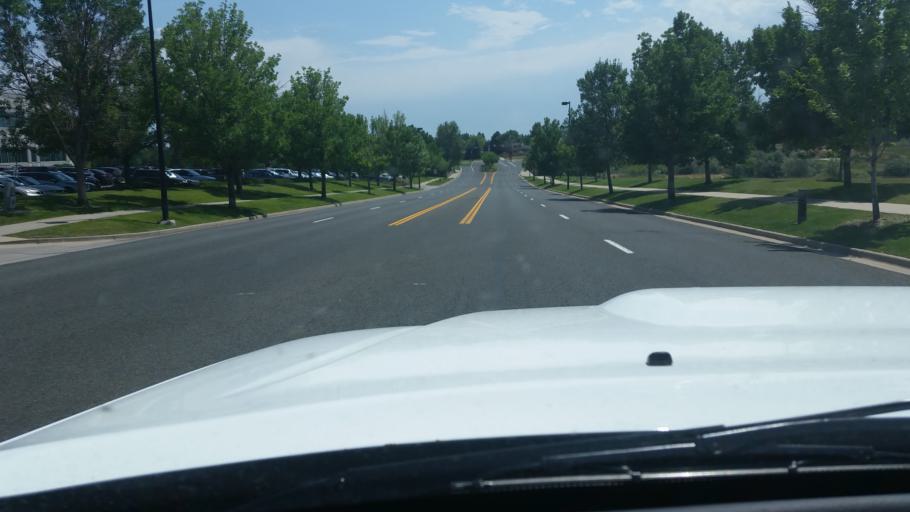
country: US
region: Colorado
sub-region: Broomfield County
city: Broomfield
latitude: 39.8959
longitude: -105.1111
